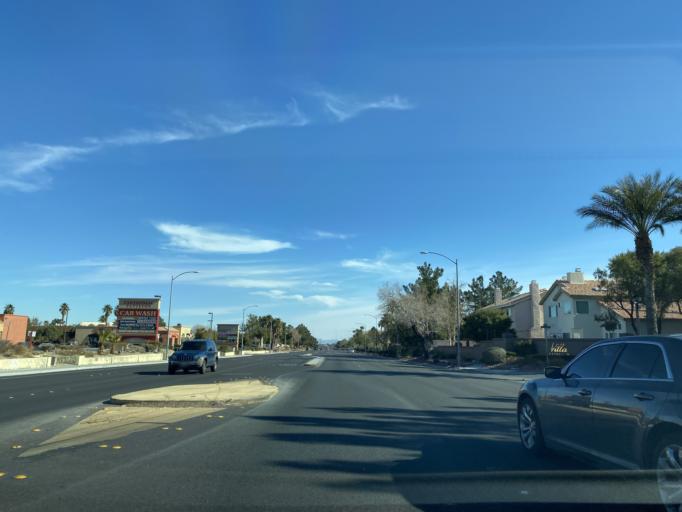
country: US
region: Nevada
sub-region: Clark County
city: Spring Valley
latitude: 36.2630
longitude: -115.2674
